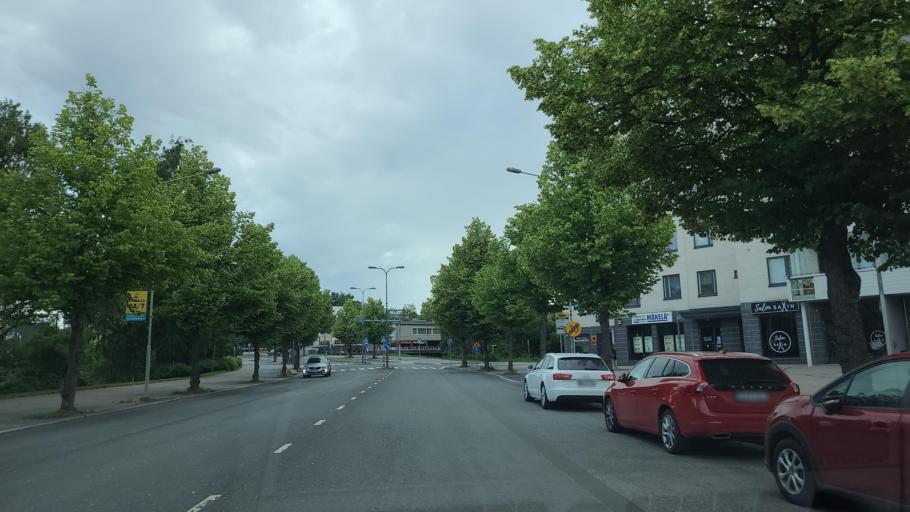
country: FI
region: Pirkanmaa
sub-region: Tampere
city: Nokia
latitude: 61.4801
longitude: 23.5102
